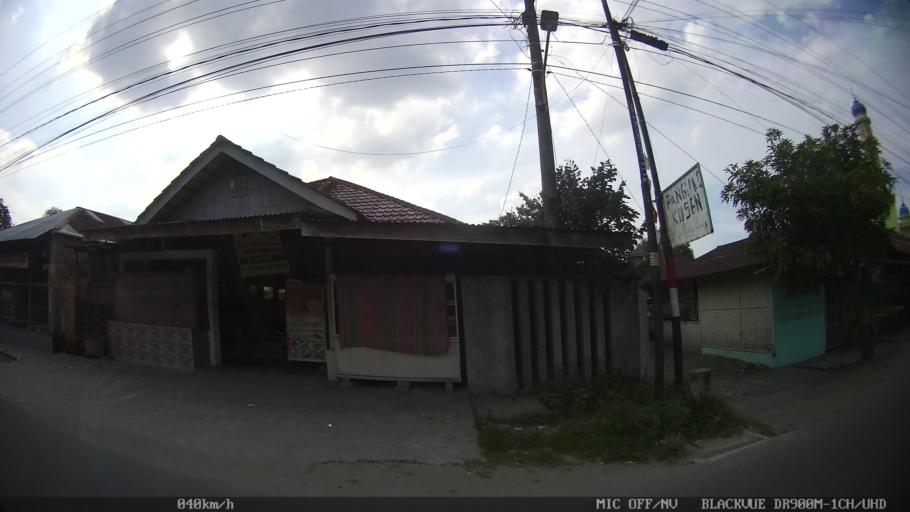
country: ID
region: North Sumatra
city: Binjai
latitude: 3.6402
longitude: 98.4946
